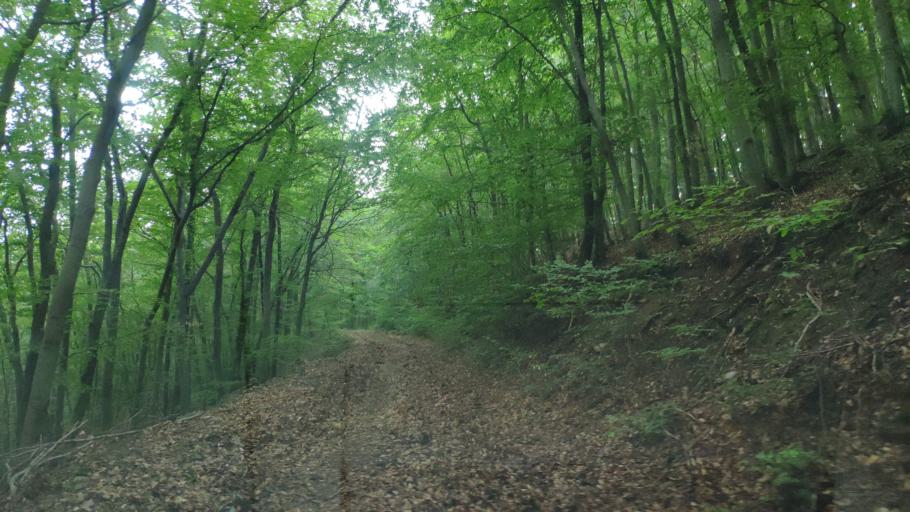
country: SK
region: Presovsky
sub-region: Okres Presov
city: Presov
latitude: 48.8673
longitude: 21.2242
